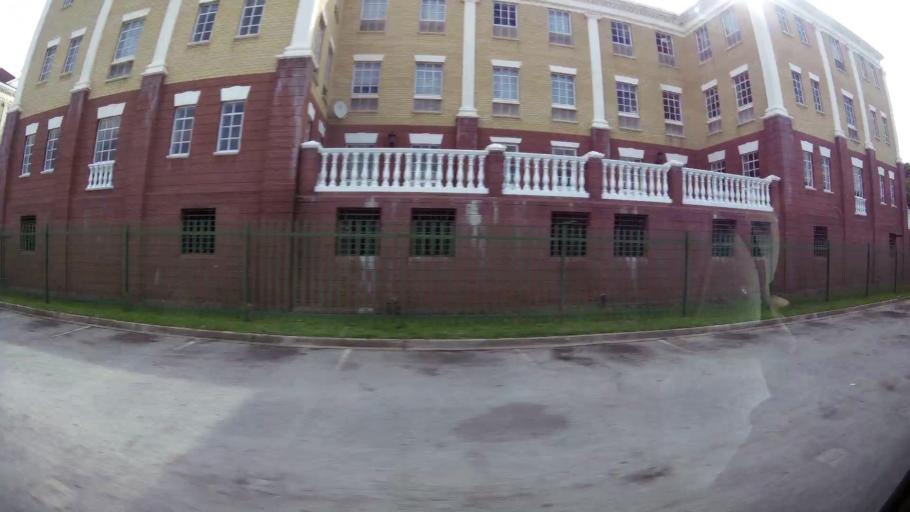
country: ZA
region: Eastern Cape
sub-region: Nelson Mandela Bay Metropolitan Municipality
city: Port Elizabeth
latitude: -33.9492
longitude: 25.5731
